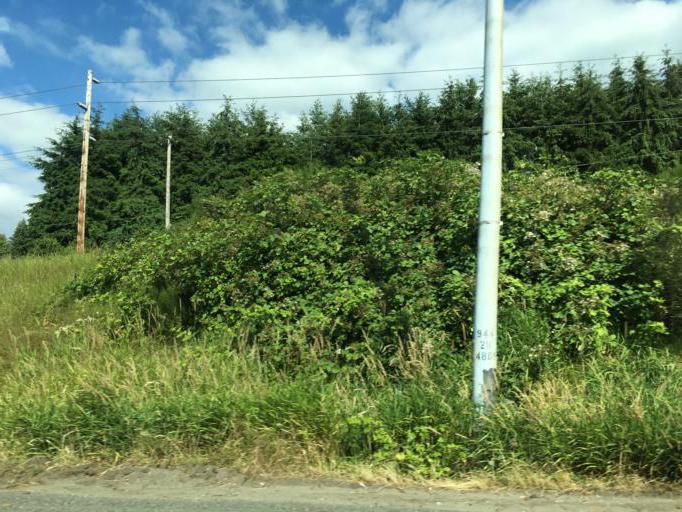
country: US
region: Washington
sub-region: Snohomish County
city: Martha Lake
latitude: 47.8377
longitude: -122.2603
